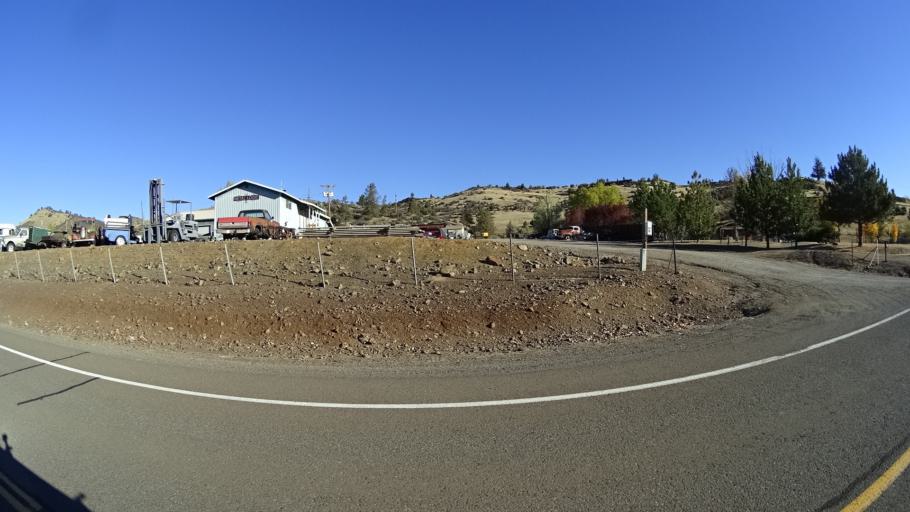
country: US
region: California
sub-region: Siskiyou County
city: Montague
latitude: 41.8978
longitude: -122.5263
